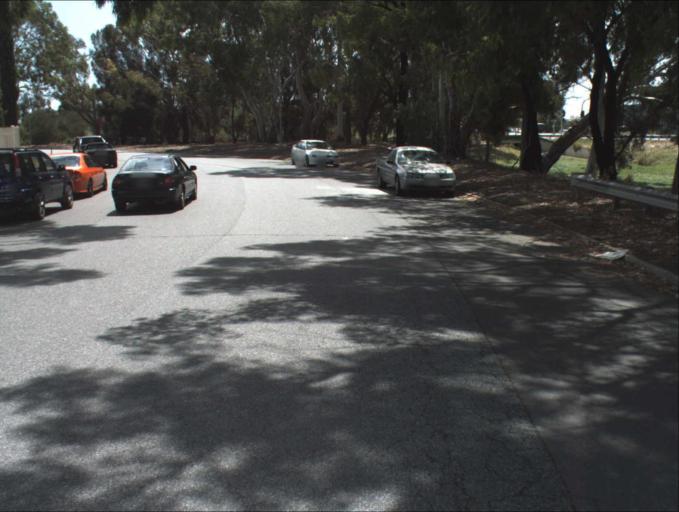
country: AU
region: South Australia
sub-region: Port Adelaide Enfield
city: Blair Athol
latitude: -34.8512
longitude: 138.5735
